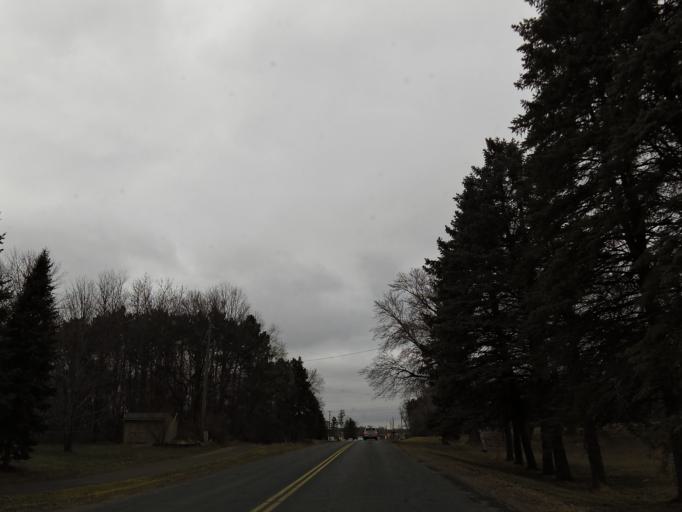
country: US
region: Minnesota
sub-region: Washington County
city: Oak Park Heights
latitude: 45.0300
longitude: -92.8225
